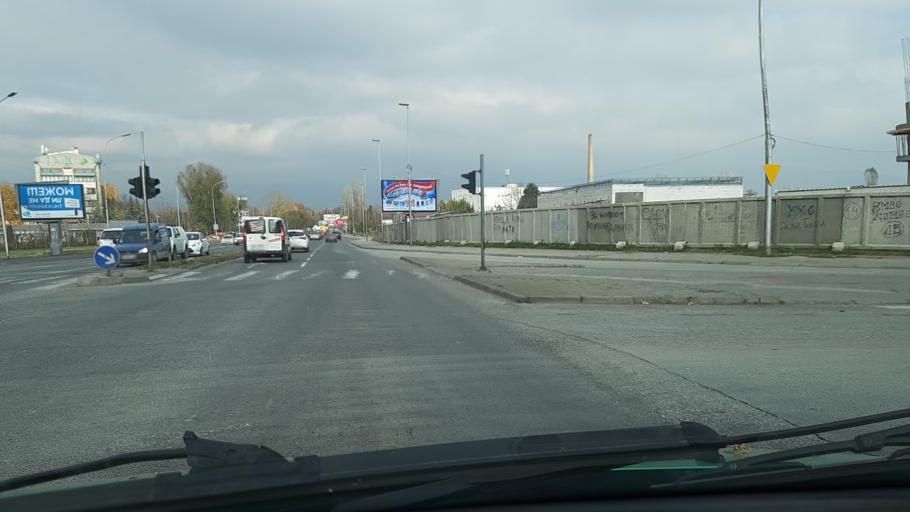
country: MK
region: Kisela Voda
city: Usje
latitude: 41.9930
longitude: 21.4752
